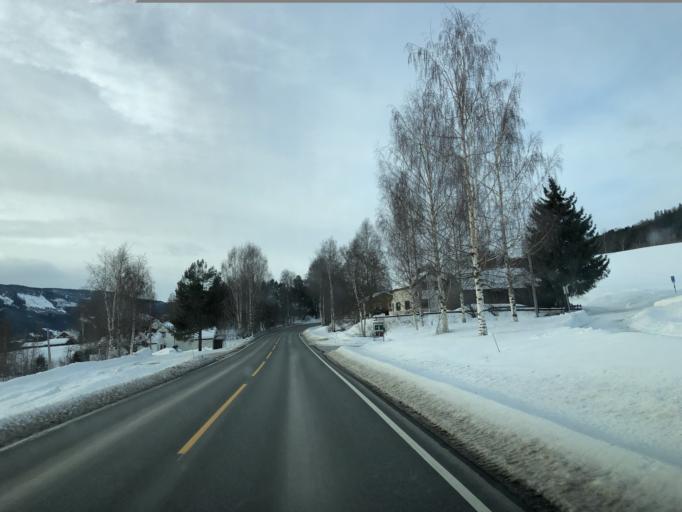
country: NO
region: Oppland
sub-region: Gausdal
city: Segalstad bru
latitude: 61.2377
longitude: 10.2040
